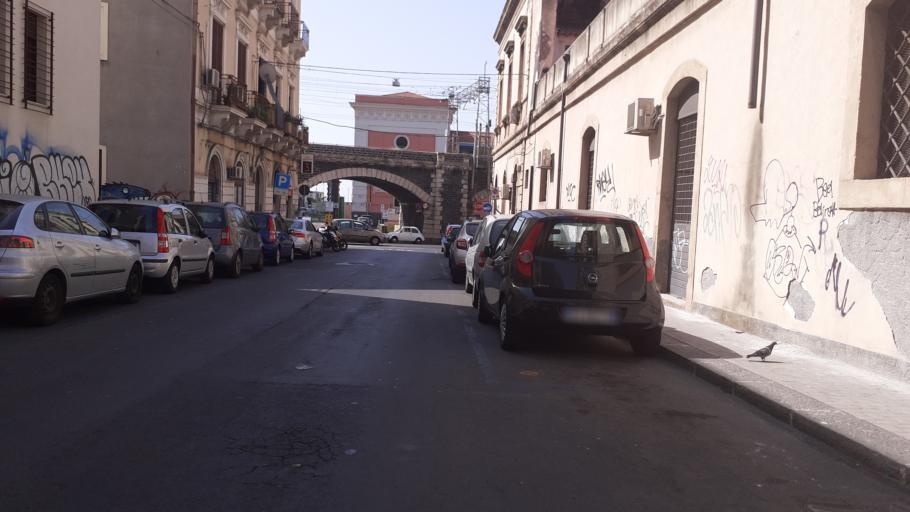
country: IT
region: Sicily
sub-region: Catania
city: Catania
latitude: 37.5019
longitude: 15.0937
